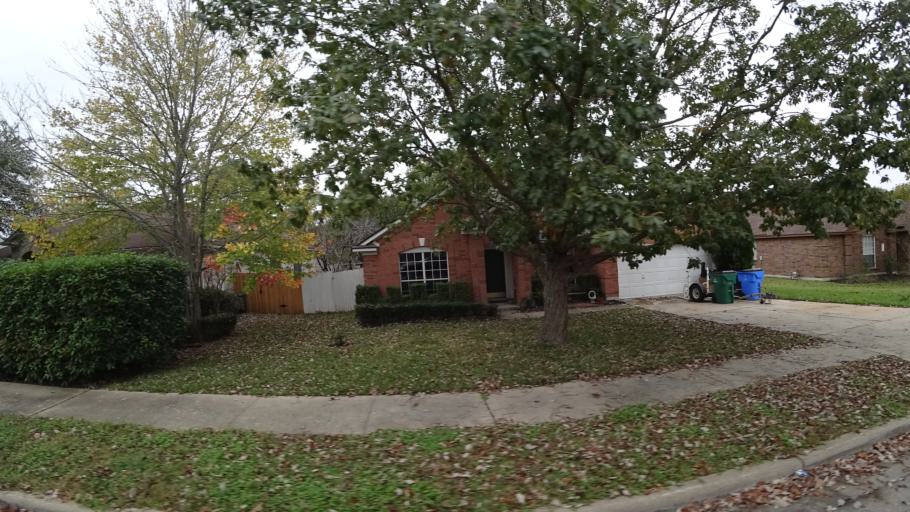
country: US
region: Texas
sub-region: Travis County
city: Pflugerville
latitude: 30.4362
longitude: -97.6077
